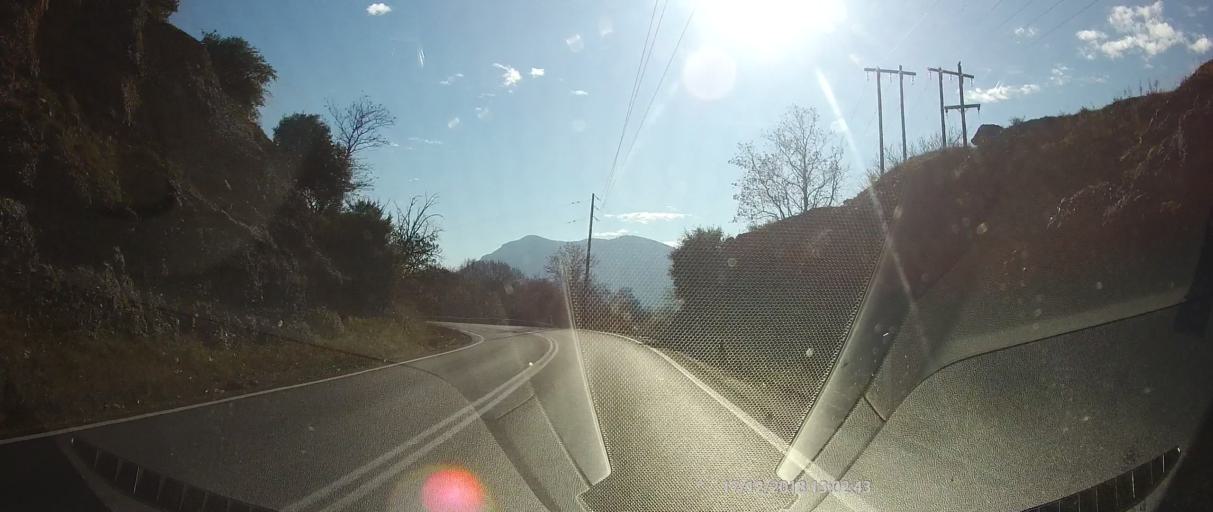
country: GR
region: Thessaly
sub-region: Trikala
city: Kastraki
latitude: 39.7200
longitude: 21.5947
